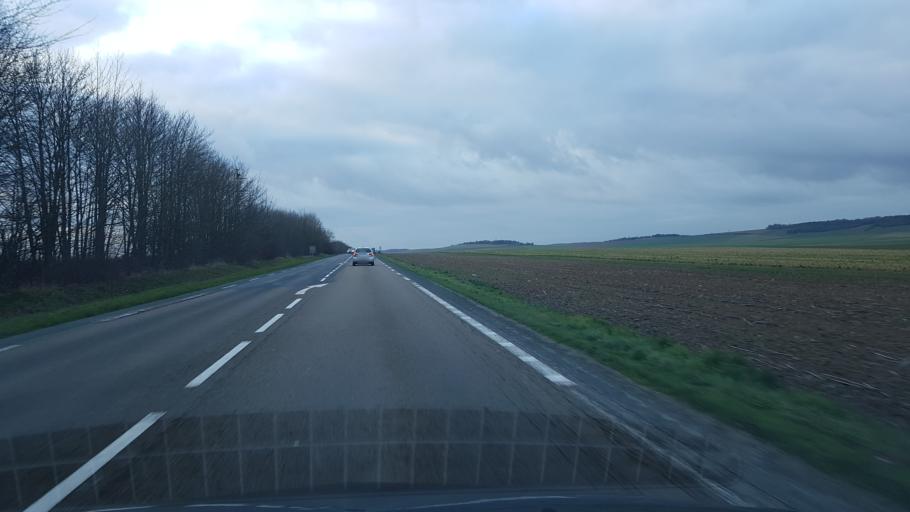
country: FR
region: Champagne-Ardenne
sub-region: Departement de la Marne
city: Sezanne
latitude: 48.7217
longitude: 3.7899
